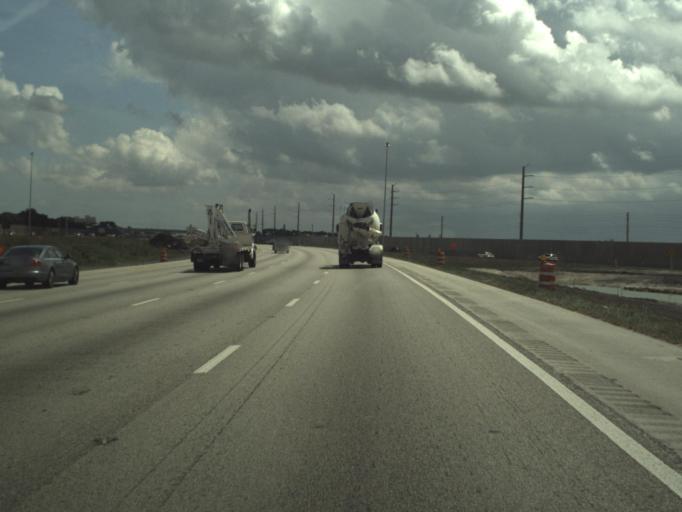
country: US
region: Florida
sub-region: Miami-Dade County
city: Palm Springs North
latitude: 25.9763
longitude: -80.3527
